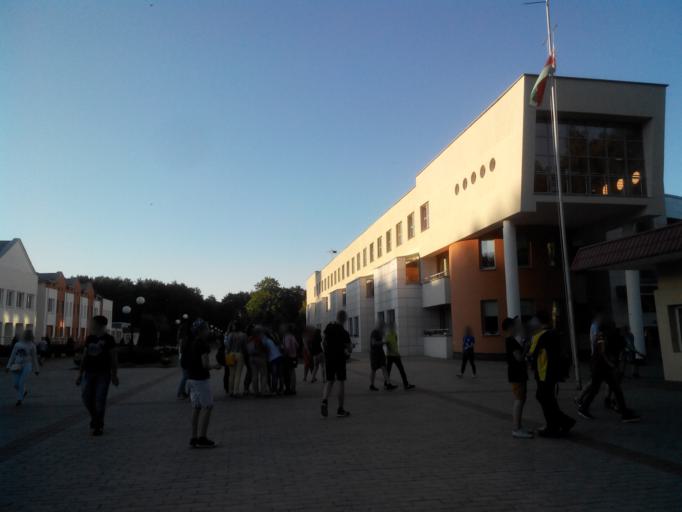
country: BY
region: Minsk
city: Narach
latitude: 54.8326
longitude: 26.7125
